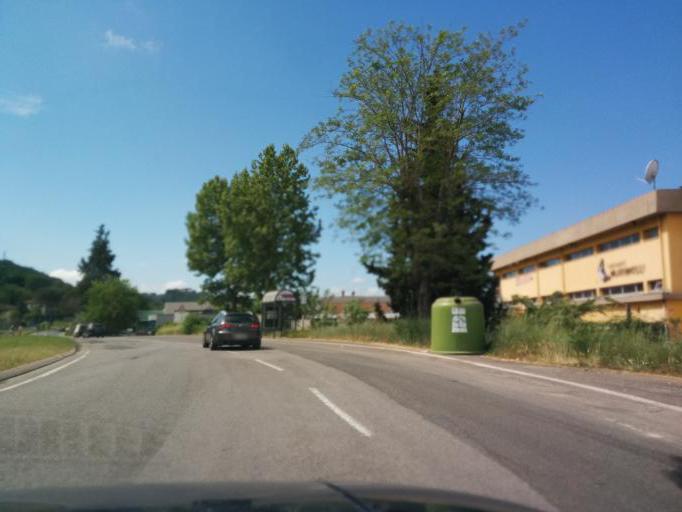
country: IT
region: Tuscany
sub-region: Provincia di Siena
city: Poggibonsi
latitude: 43.4694
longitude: 11.1266
